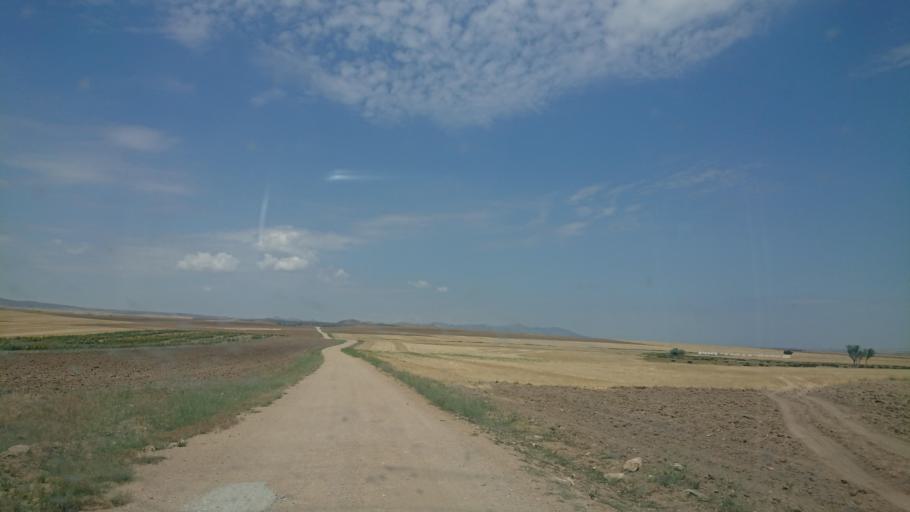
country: TR
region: Aksaray
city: Agacoren
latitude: 38.9540
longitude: 33.9386
